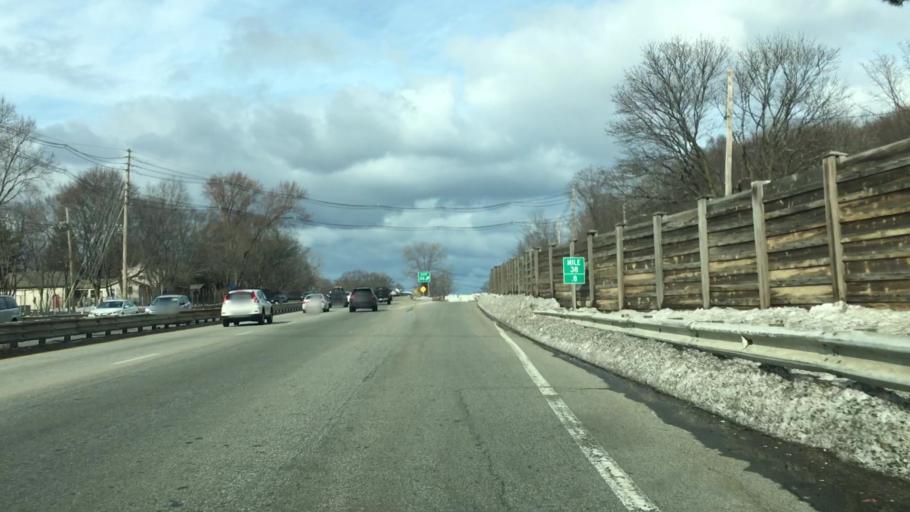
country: US
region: Massachusetts
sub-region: Essex County
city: South Peabody
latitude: 42.5313
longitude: -70.9521
